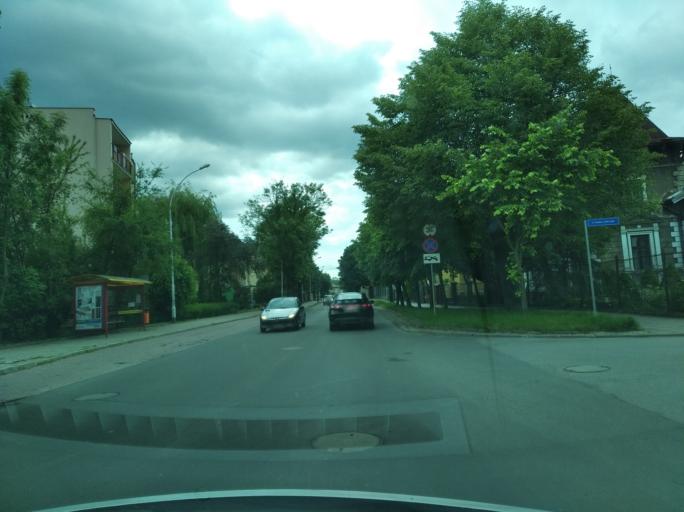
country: PL
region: Subcarpathian Voivodeship
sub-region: Przemysl
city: Przemysl
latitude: 49.7893
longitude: 22.7722
